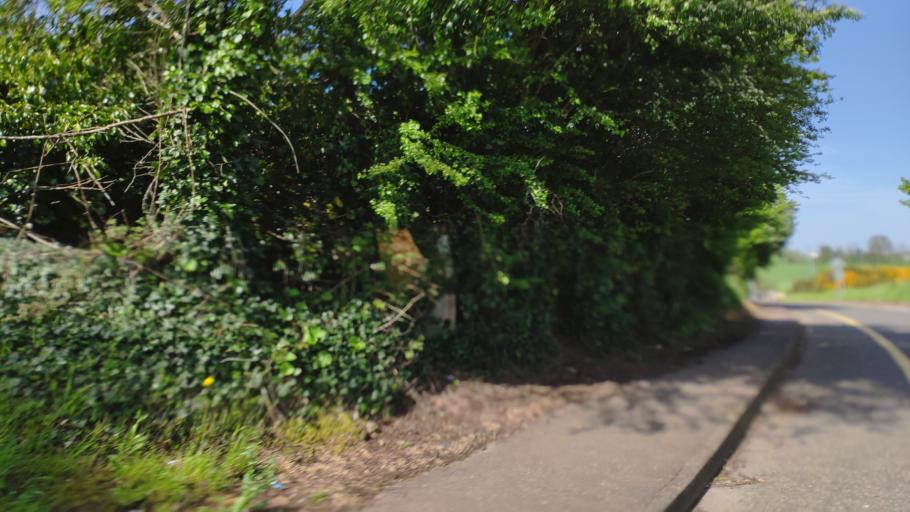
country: IE
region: Munster
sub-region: County Cork
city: Cork
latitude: 51.9236
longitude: -8.4920
